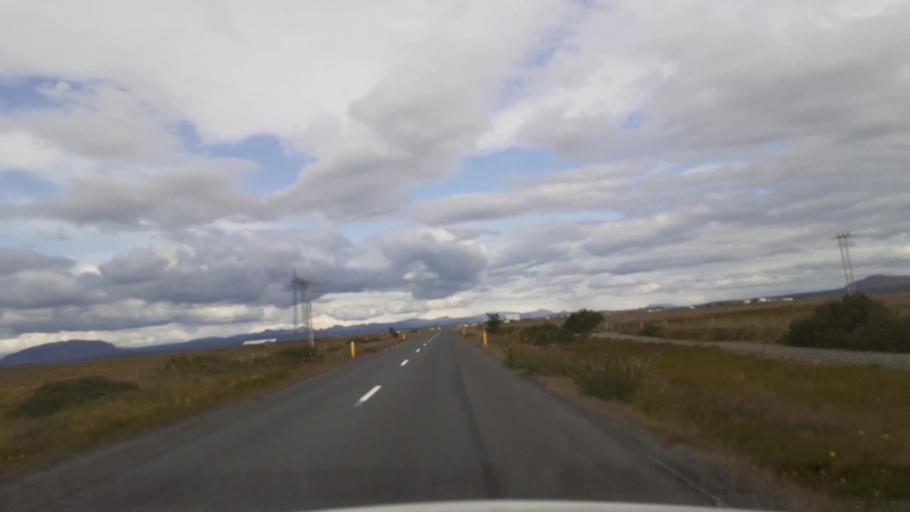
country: IS
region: South
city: Selfoss
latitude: 63.9371
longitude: -20.8403
